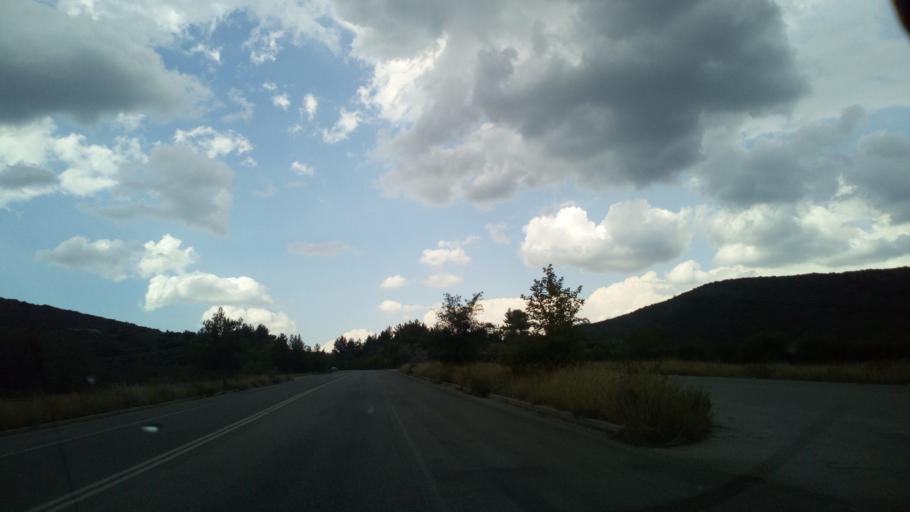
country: GR
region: Central Macedonia
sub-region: Nomos Chalkidikis
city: Polygyros
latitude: 40.3489
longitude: 23.4480
